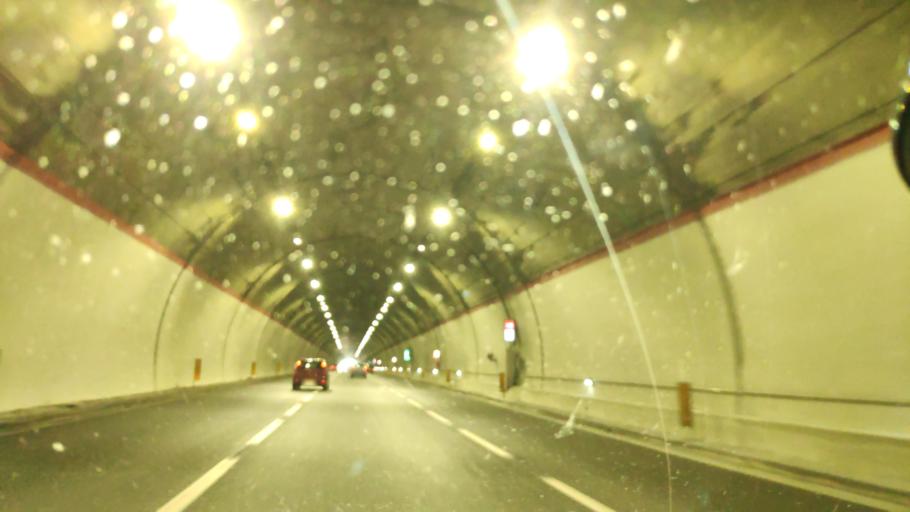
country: IT
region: Campania
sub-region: Provincia di Salerno
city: Pezzano-Filetta
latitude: 40.6744
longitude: 14.8576
